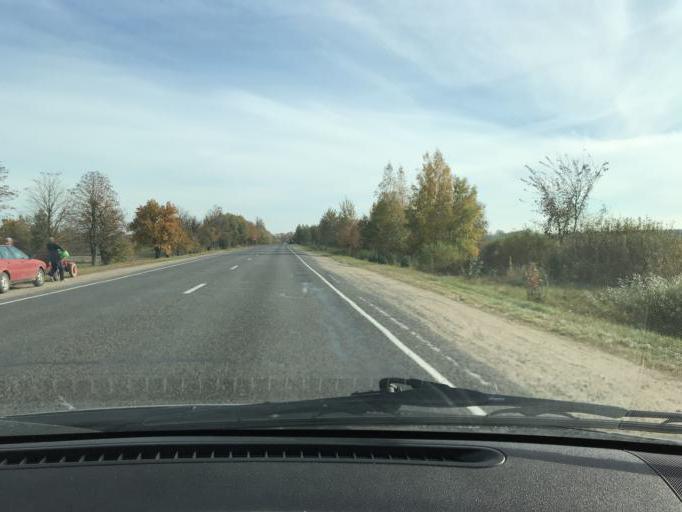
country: BY
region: Brest
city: Asnyezhytsy
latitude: 52.2033
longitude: 26.0590
